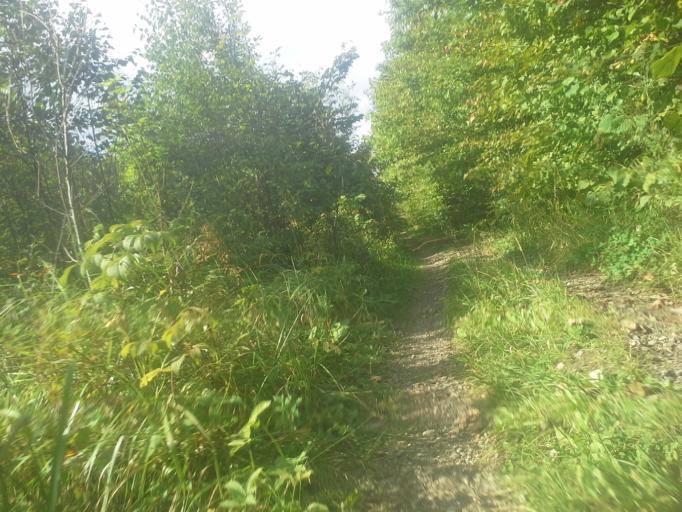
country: RU
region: Moskovskaya
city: Kievskij
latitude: 55.3438
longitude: 36.9383
